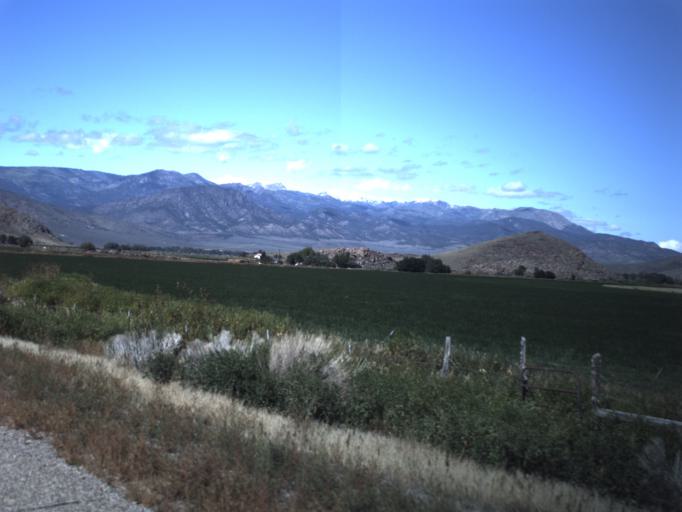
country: US
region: Utah
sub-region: Piute County
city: Junction
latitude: 38.2082
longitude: -112.1833
